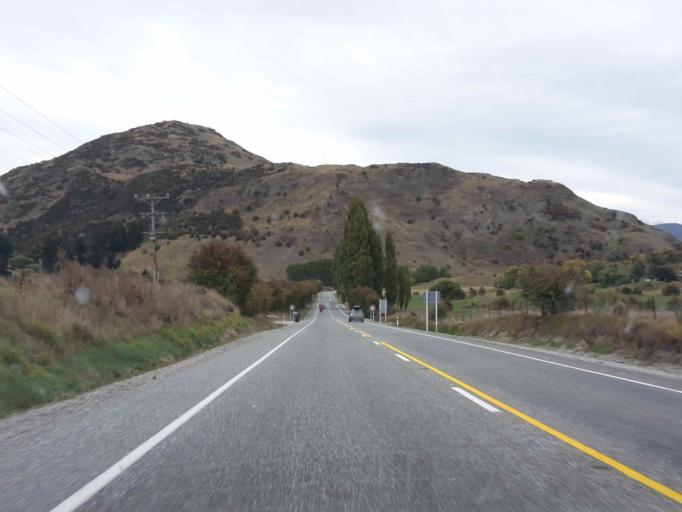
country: NZ
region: Otago
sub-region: Queenstown-Lakes District
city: Arrowtown
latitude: -44.9790
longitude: 168.8463
